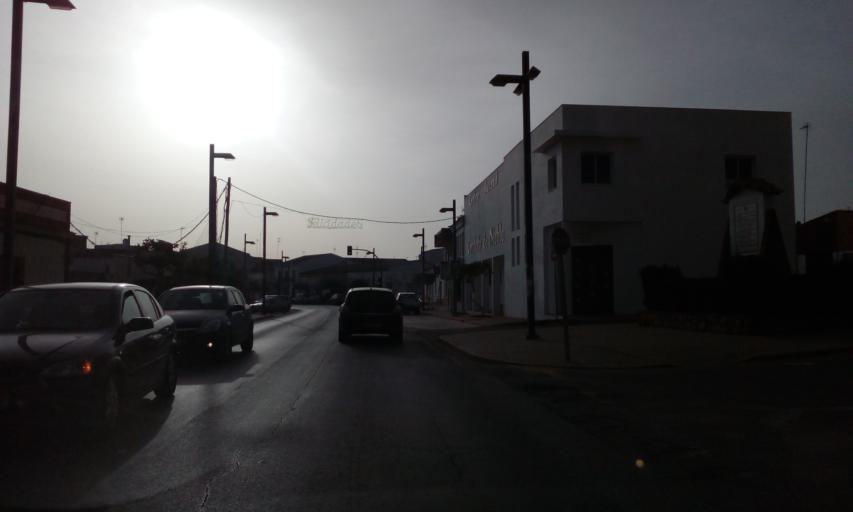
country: ES
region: Andalusia
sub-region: Provincia de Huelva
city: Niebla
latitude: 37.3648
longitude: -6.6766
